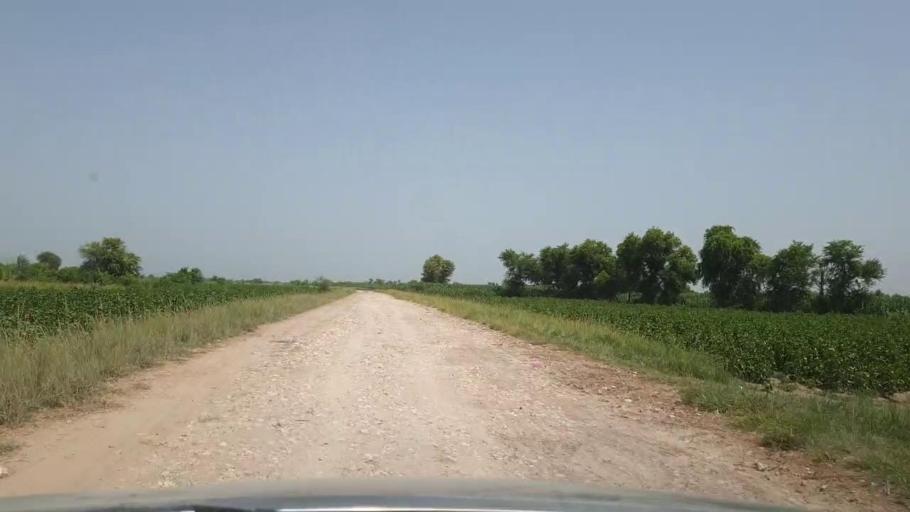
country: PK
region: Sindh
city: Pano Aqil
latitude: 27.8074
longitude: 69.2363
